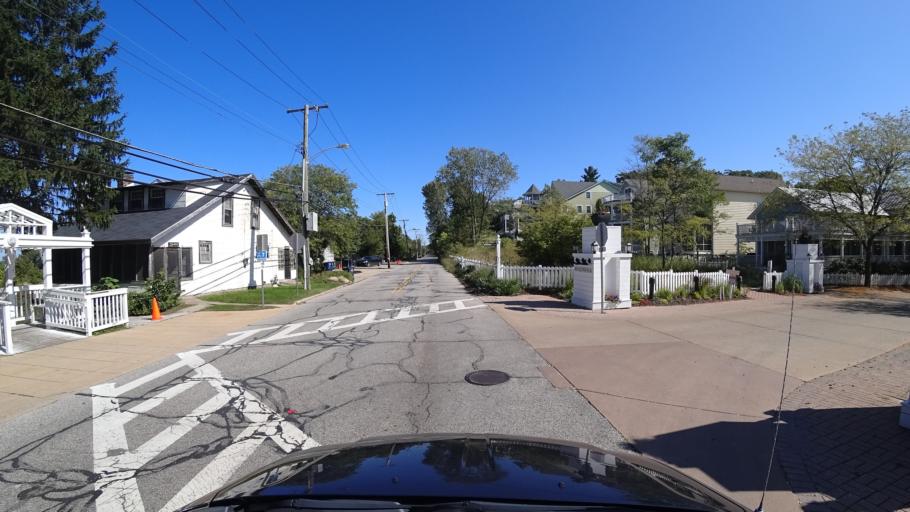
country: US
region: Indiana
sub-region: LaPorte County
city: Michigan City
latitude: 41.7321
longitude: -86.8845
